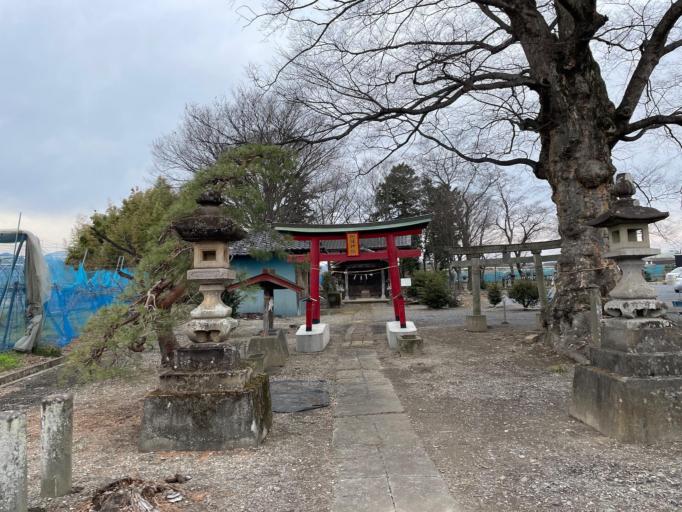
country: JP
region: Gunma
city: Fujioka
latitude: 36.2265
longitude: 139.1010
